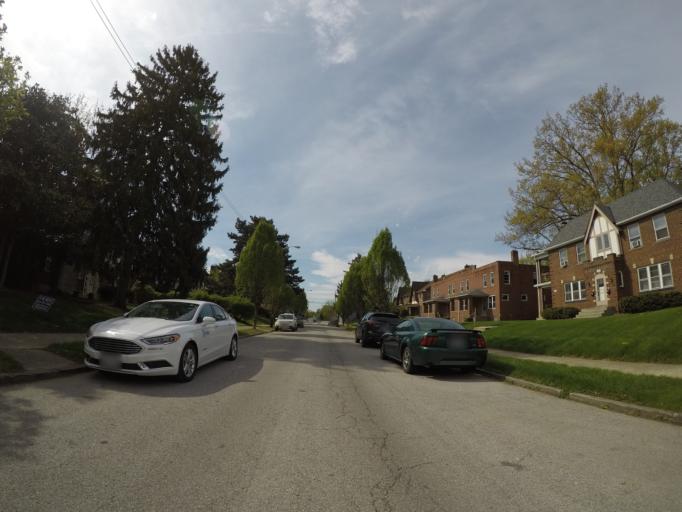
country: US
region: Ohio
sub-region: Franklin County
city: Upper Arlington
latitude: 39.9905
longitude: -83.0552
